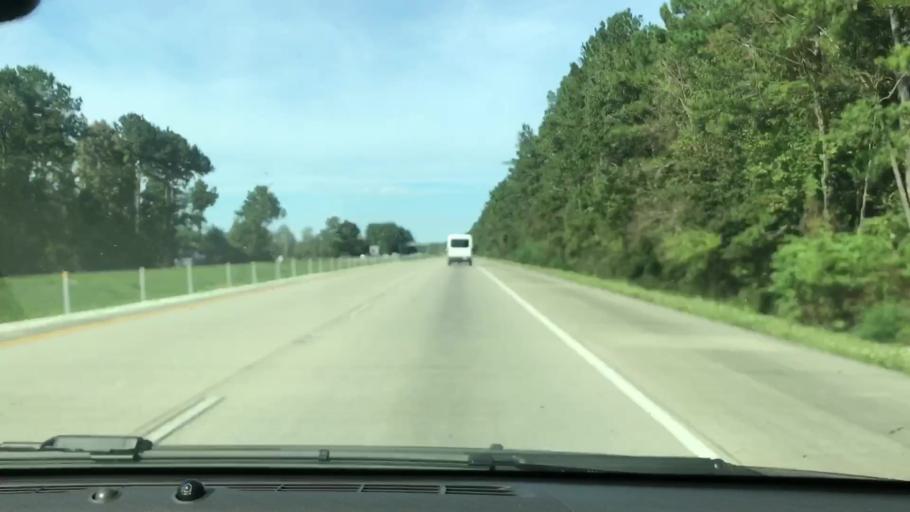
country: US
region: Louisiana
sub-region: Saint Tammany Parish
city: Pearl River
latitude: 30.3279
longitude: -89.7376
